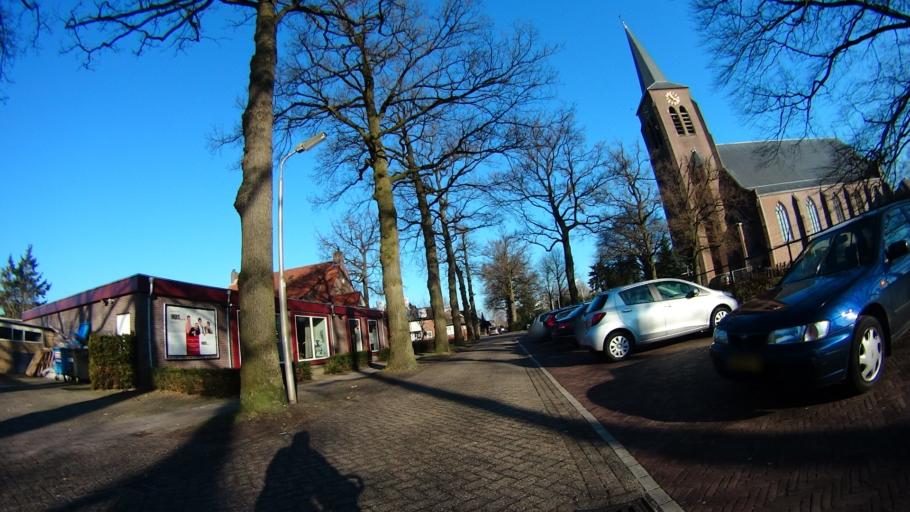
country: NL
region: Utrecht
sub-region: Gemeente Amersfoort
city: Hoogland
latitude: 52.1898
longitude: 5.3831
